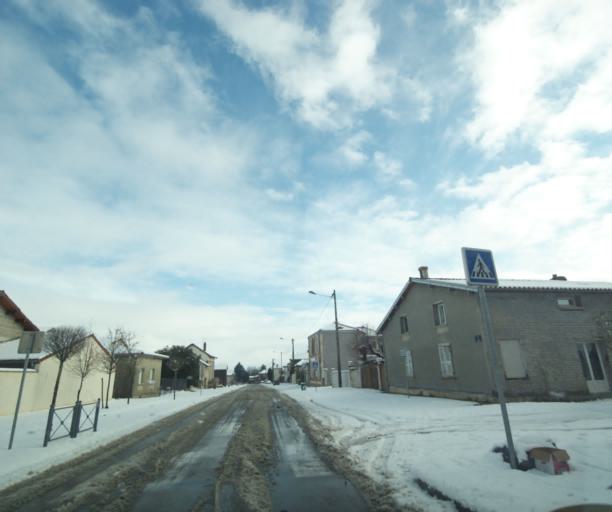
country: FR
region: Champagne-Ardenne
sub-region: Departement de la Haute-Marne
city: Montier-en-Der
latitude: 48.4548
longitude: 4.6895
